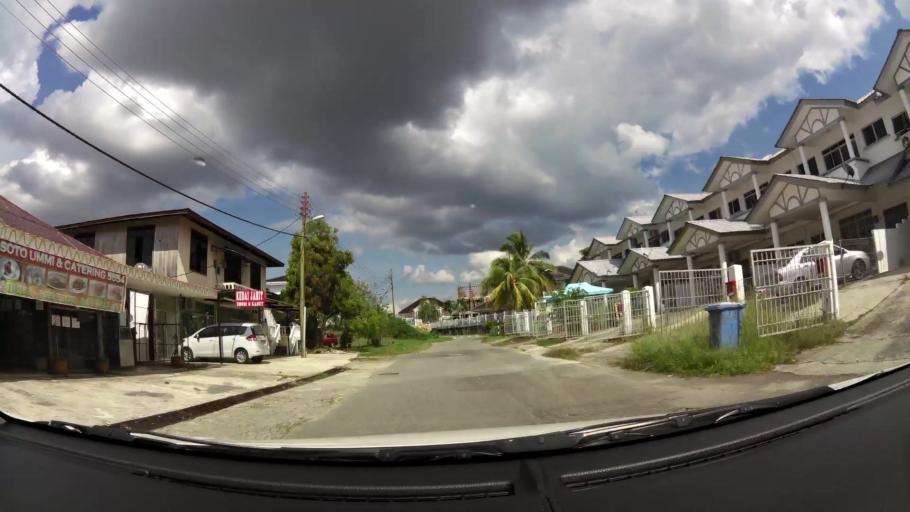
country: BN
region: Brunei and Muara
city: Bandar Seri Begawan
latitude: 4.9560
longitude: 114.9607
